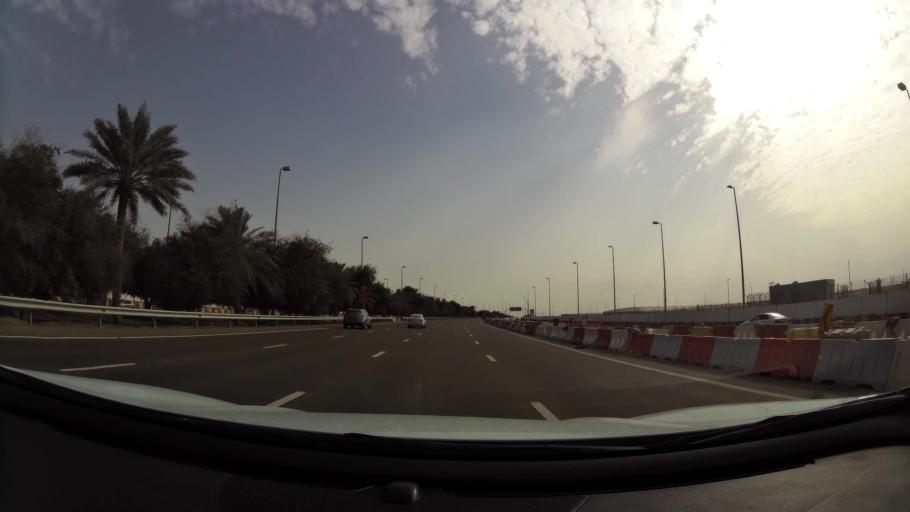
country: AE
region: Abu Dhabi
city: Abu Dhabi
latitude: 24.4199
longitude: 54.6770
